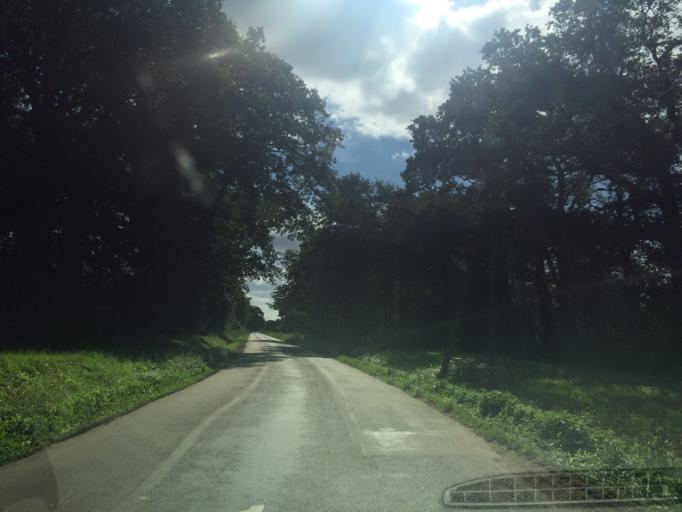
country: FR
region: Pays de la Loire
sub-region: Departement de la Loire-Atlantique
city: Chemere
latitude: 47.1576
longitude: -1.9023
